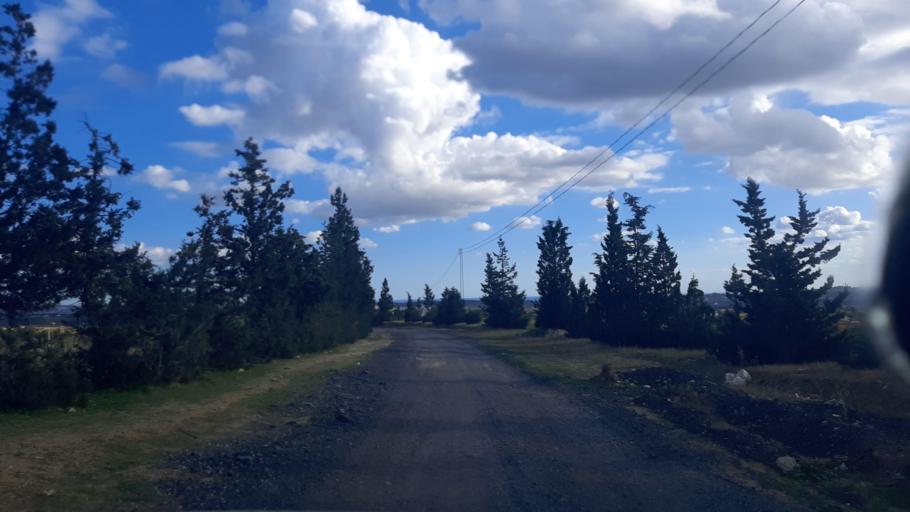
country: TN
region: Nabul
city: Bu `Urqub
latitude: 36.4698
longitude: 10.4768
